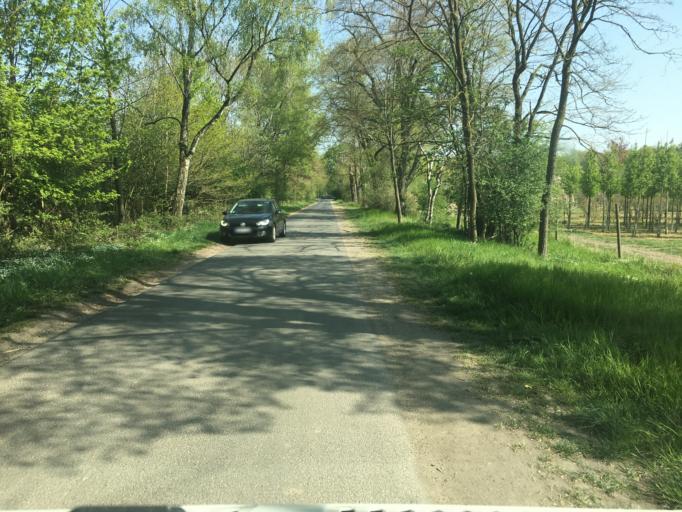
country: DE
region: North Rhine-Westphalia
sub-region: Regierungsbezirk Koln
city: Frechen
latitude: 50.9338
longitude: 6.7414
